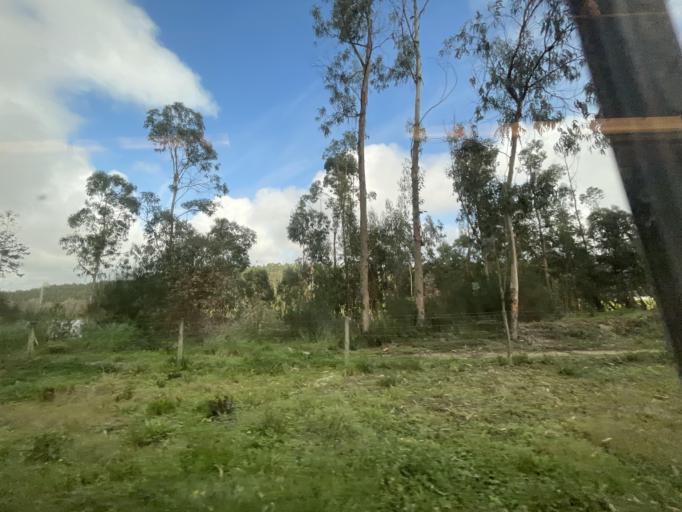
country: PT
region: Porto
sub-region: Vila do Conde
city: Vila do Conde
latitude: 41.3499
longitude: -8.7294
